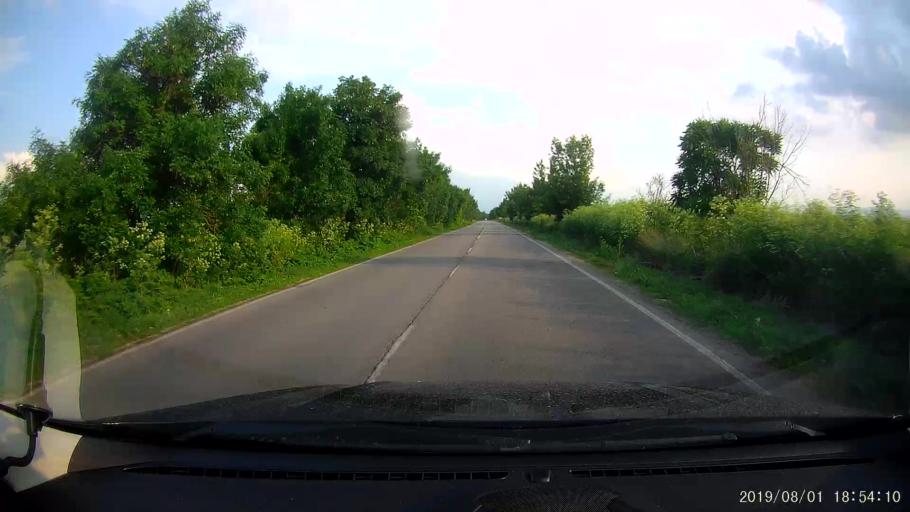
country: BG
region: Shumen
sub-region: Obshtina Shumen
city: Shumen
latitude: 43.2052
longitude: 27.0000
